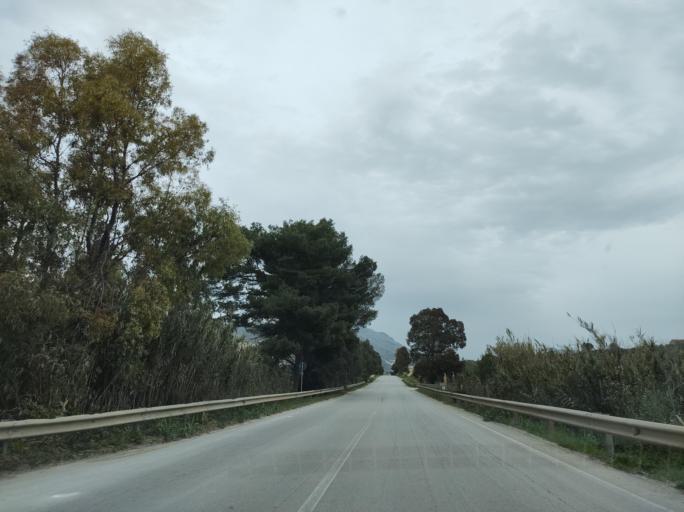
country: IT
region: Sicily
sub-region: Trapani
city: Custonaci
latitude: 38.0414
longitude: 12.6745
